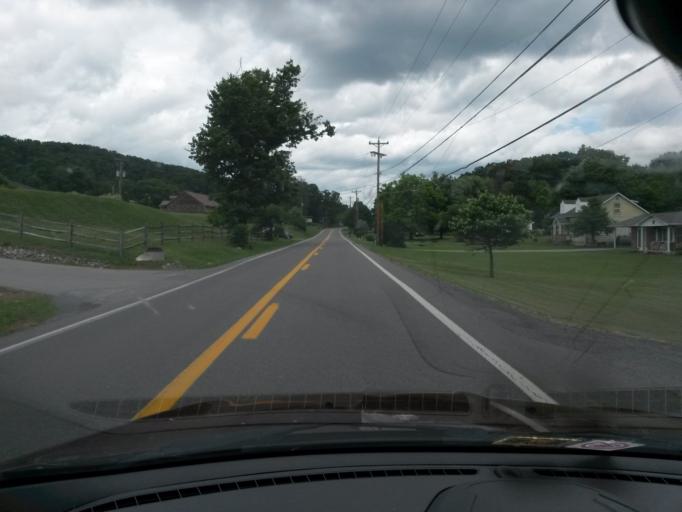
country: US
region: Virginia
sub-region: Giles County
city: Pearisburg
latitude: 37.4079
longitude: -80.7566
